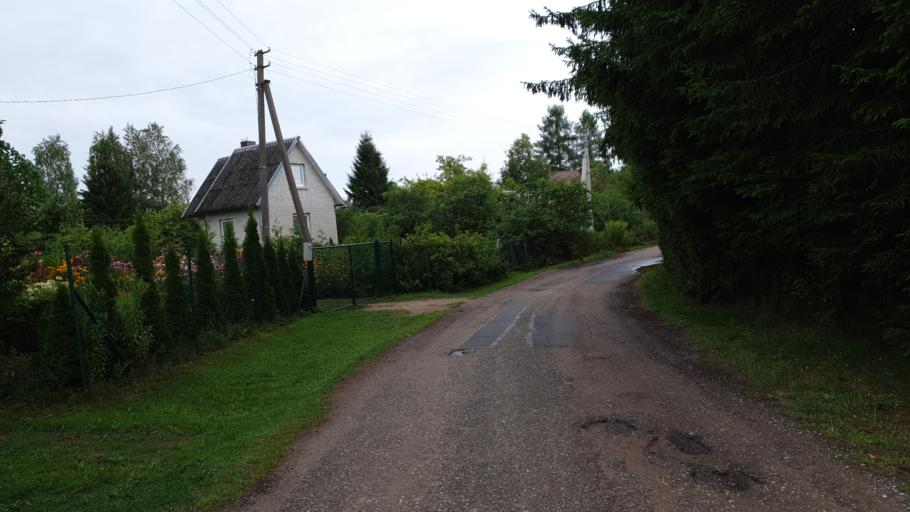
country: LT
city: Grigiskes
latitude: 54.7671
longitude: 25.0163
